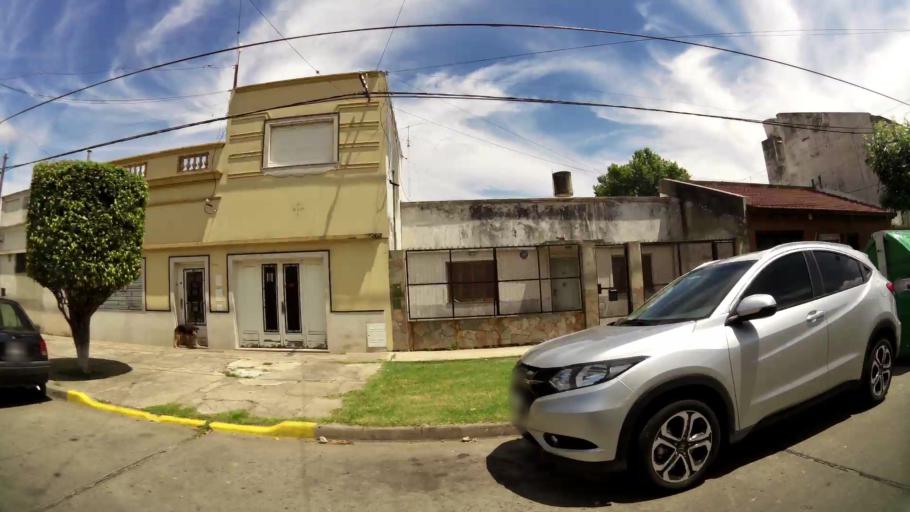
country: AR
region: Santa Fe
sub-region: Departamento de Rosario
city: Rosario
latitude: -32.9765
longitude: -60.6297
